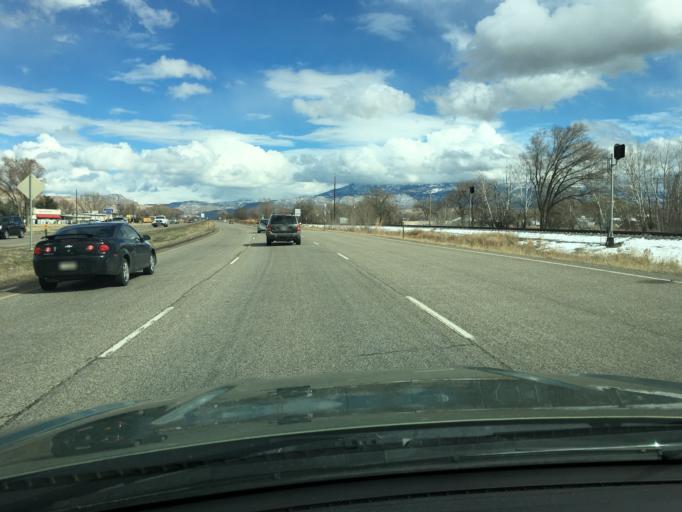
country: US
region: Colorado
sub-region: Mesa County
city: Fruitvale
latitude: 39.0779
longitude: -108.4932
